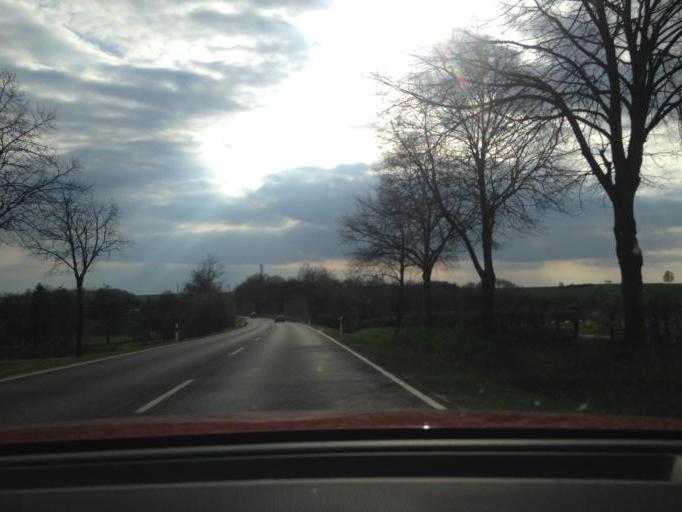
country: DE
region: Bavaria
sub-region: Upper Palatinate
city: Kemnath
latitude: 49.8774
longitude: 11.8828
